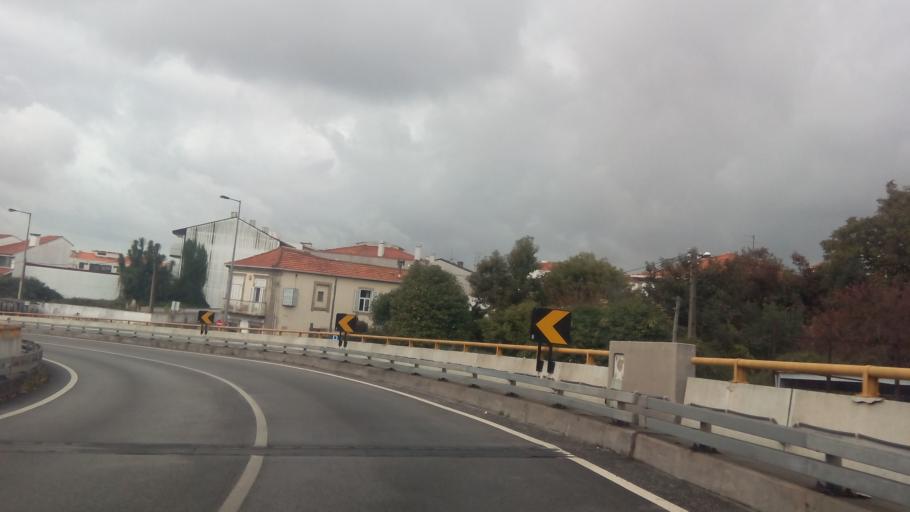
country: PT
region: Porto
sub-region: Maia
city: Pedroucos
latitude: 41.1814
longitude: -8.5839
